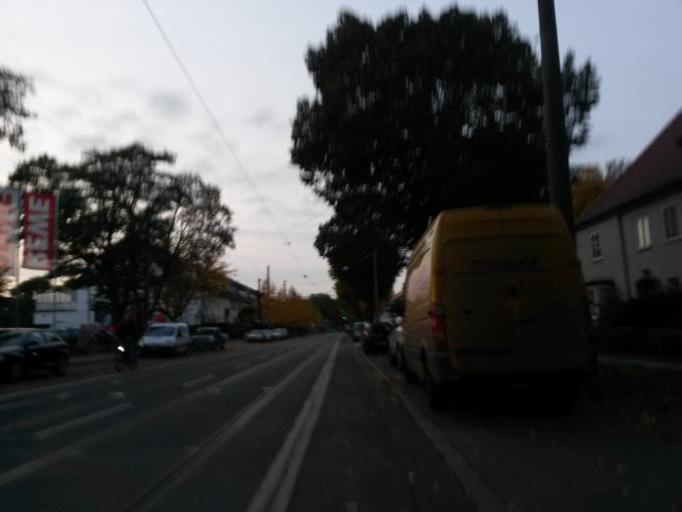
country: DE
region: Bremen
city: Bremen
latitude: 53.0666
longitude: 8.8581
